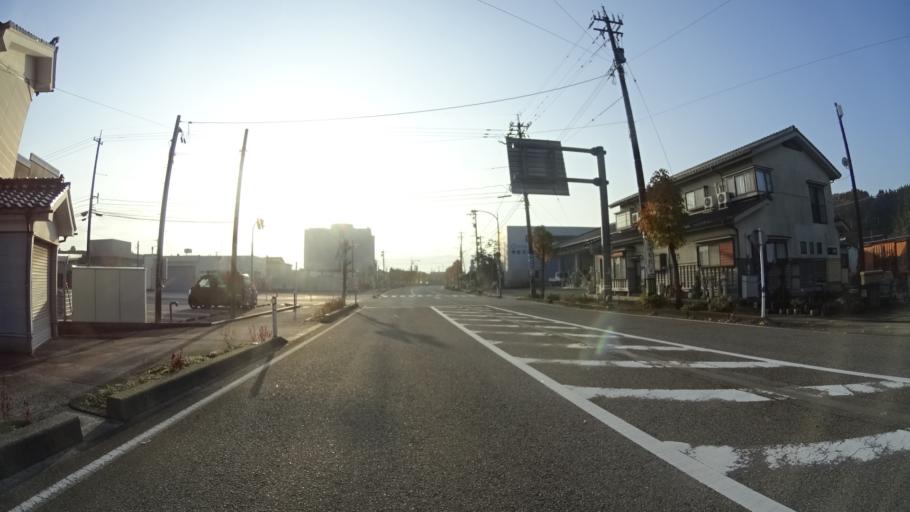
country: JP
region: Ishikawa
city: Nanao
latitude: 37.0561
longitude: 136.9535
